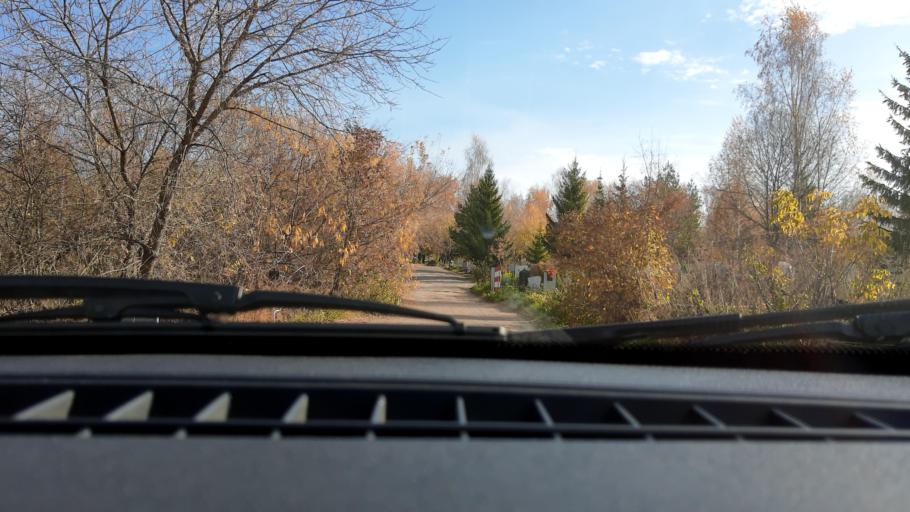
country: RU
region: Bashkortostan
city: Ufa
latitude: 54.8508
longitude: 56.1523
